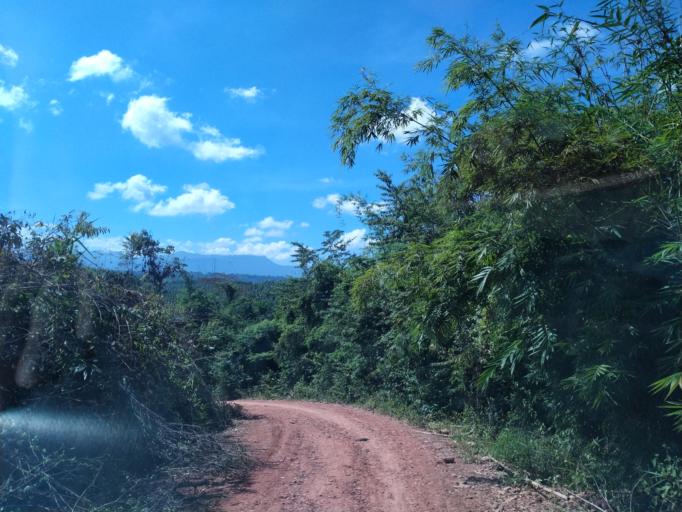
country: LA
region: Vientiane
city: Muang Phon-Hong
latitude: 18.6138
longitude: 102.8511
